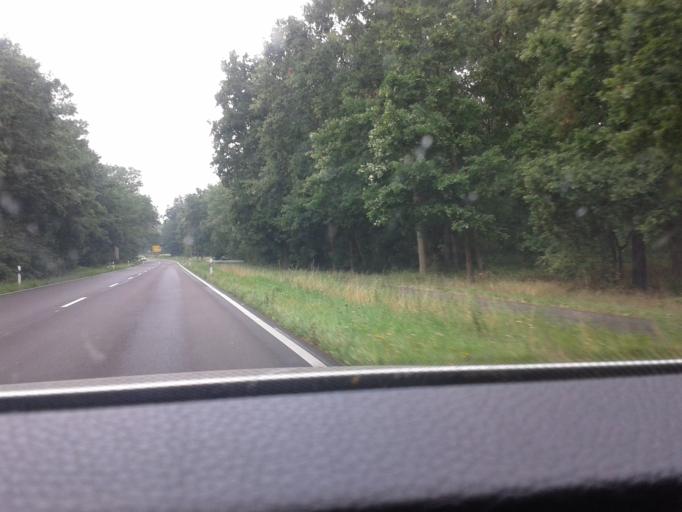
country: DE
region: Lower Saxony
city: Sassenburg
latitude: 52.4966
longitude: 10.6164
